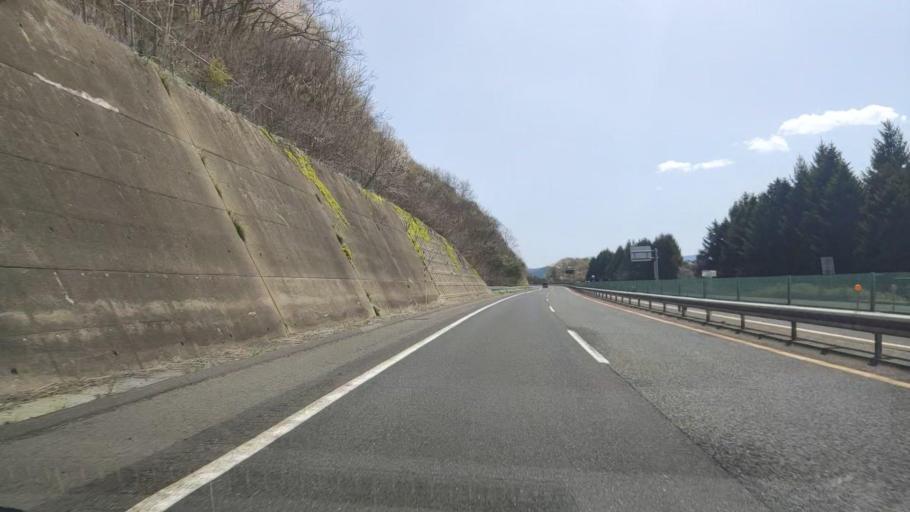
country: JP
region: Iwate
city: Ichinohe
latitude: 40.2324
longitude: 141.3016
